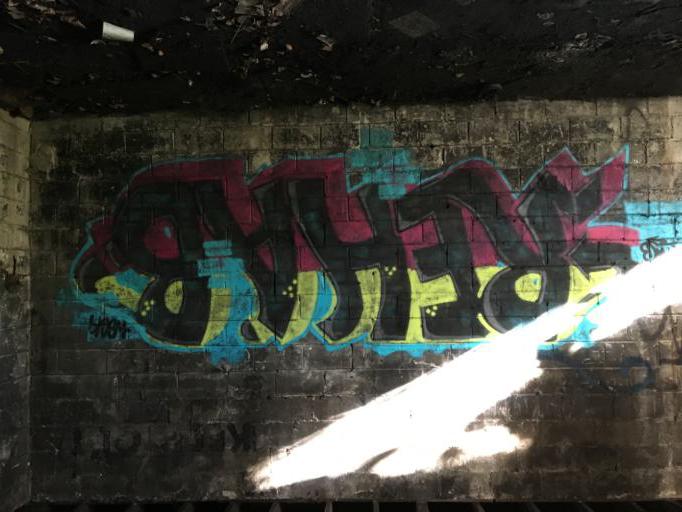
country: US
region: Michigan
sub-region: Wayne County
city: Hamtramck
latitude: 42.3852
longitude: -83.0700
